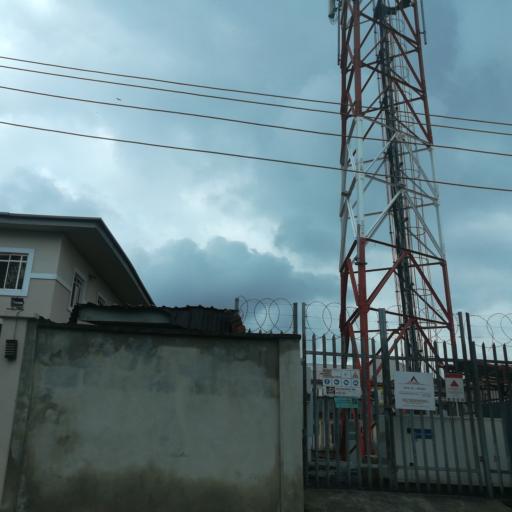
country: NG
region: Lagos
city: Ikoyi
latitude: 6.4387
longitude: 3.4583
